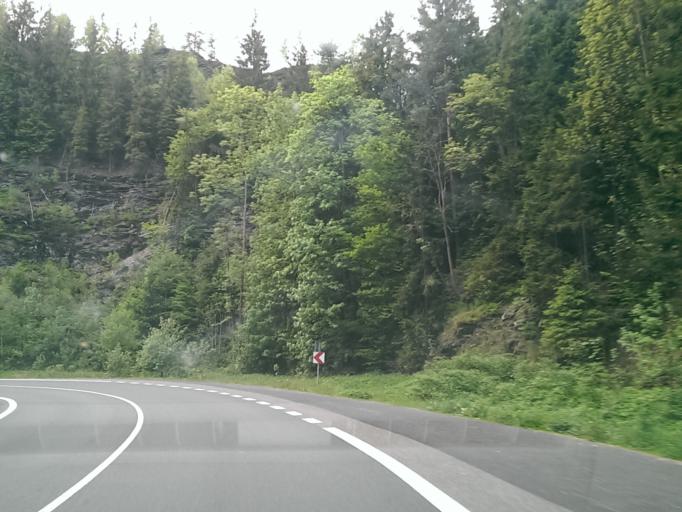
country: CZ
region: Liberecky
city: Zelezny Brod
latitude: 50.6643
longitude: 15.2632
